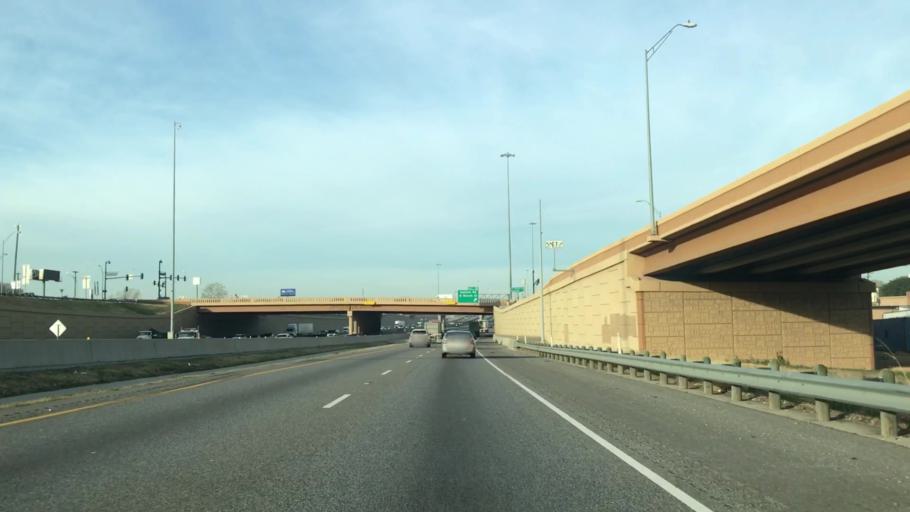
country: US
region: Texas
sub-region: Tarrant County
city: Watauga
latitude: 32.8399
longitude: -97.2620
